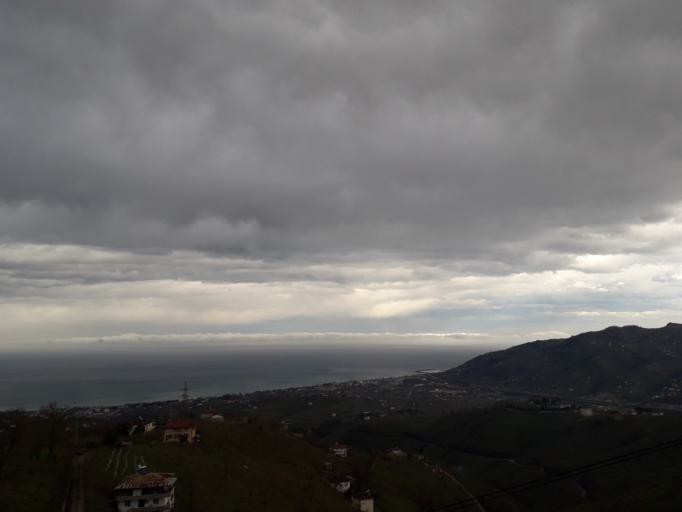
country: TR
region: Ordu
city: Ordu
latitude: 41.0089
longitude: 37.8267
